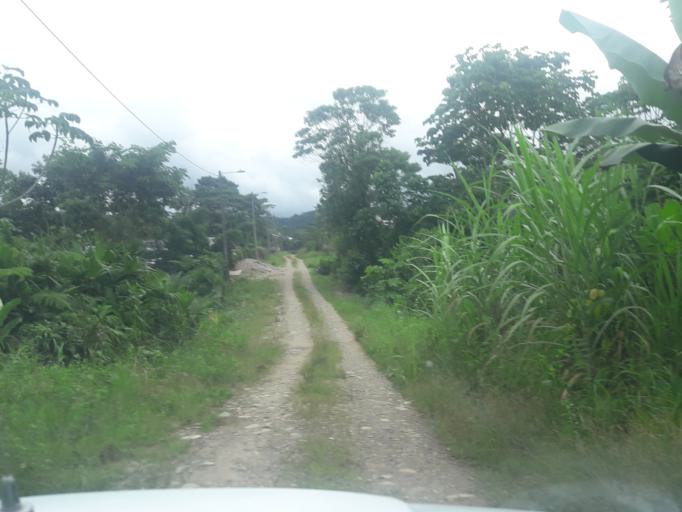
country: EC
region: Napo
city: Archidona
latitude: -0.9487
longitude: -77.8148
